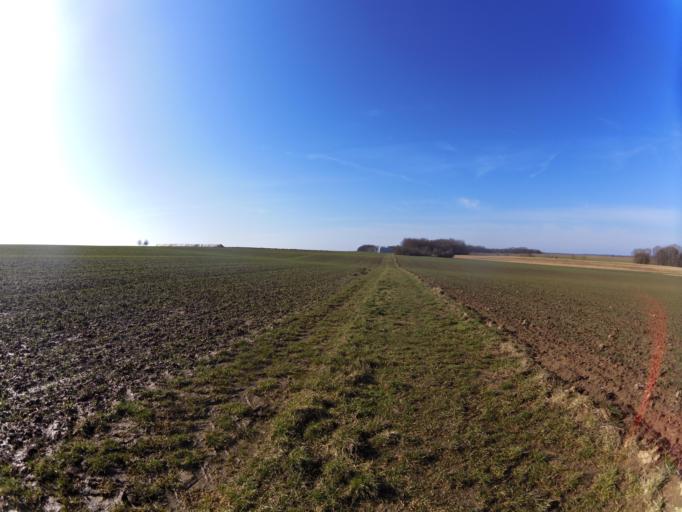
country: DE
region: Bavaria
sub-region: Regierungsbezirk Unterfranken
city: Giebelstadt
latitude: 49.6868
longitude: 9.9675
